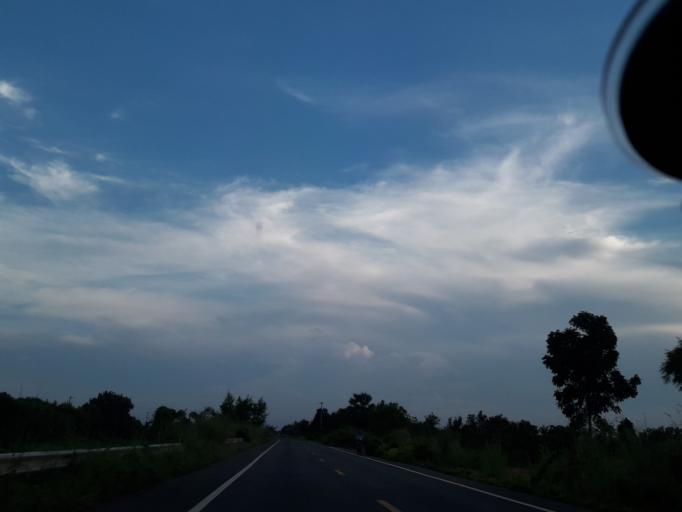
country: TH
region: Sara Buri
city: Nong Khae
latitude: 14.2950
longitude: 100.8911
